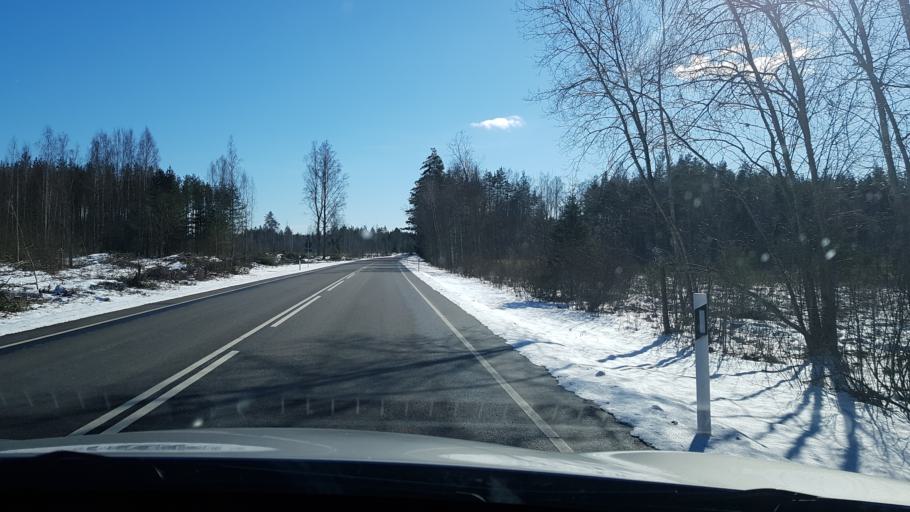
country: EE
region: Polvamaa
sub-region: Raepina vald
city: Rapina
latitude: 57.9887
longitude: 27.5640
